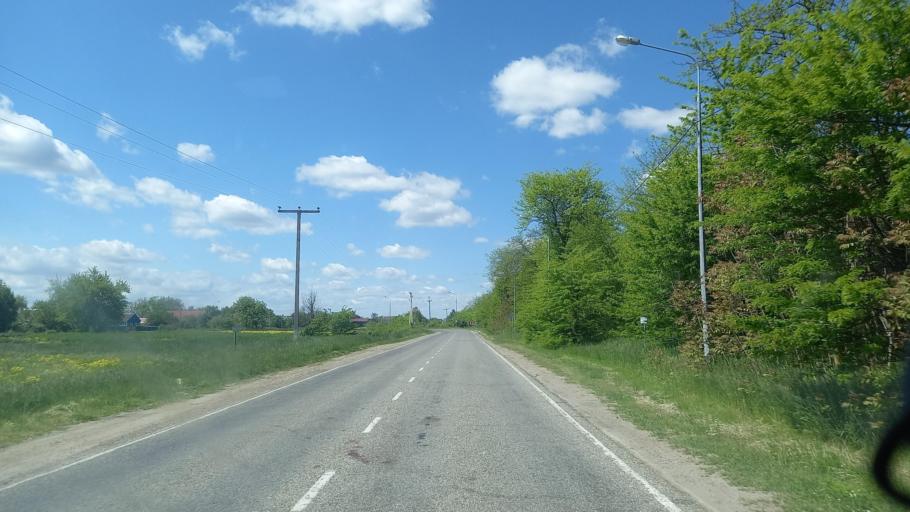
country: RU
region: Krasnodarskiy
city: Tbilisskaya
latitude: 45.3356
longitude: 40.3001
